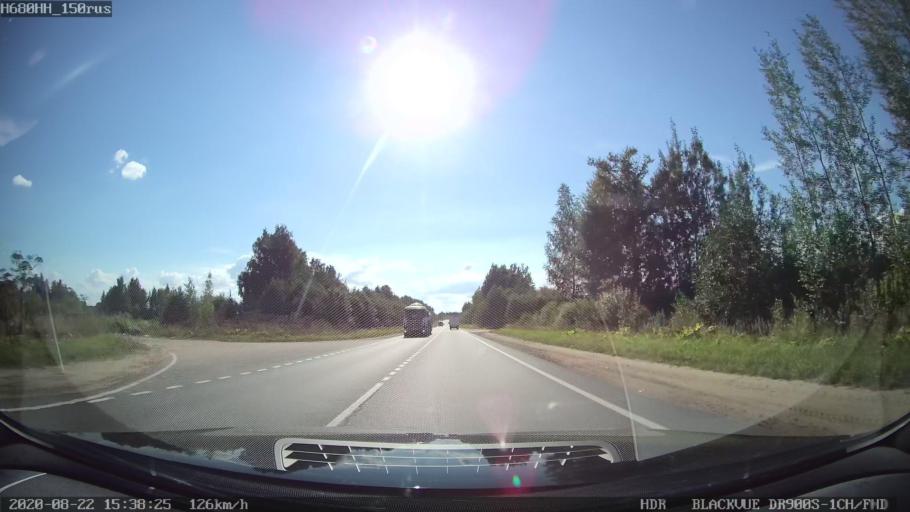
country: RU
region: Tverskaya
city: Bezhetsk
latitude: 57.7626
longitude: 36.6488
